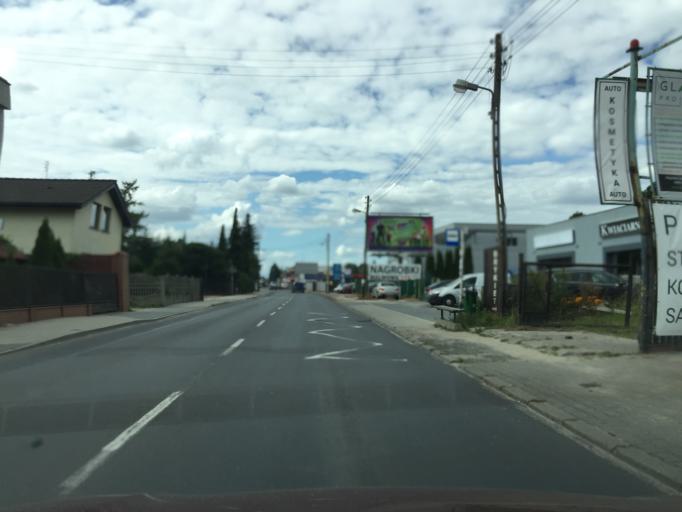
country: PL
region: Greater Poland Voivodeship
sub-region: Powiat poznanski
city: Plewiska
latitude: 52.3867
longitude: 16.8186
